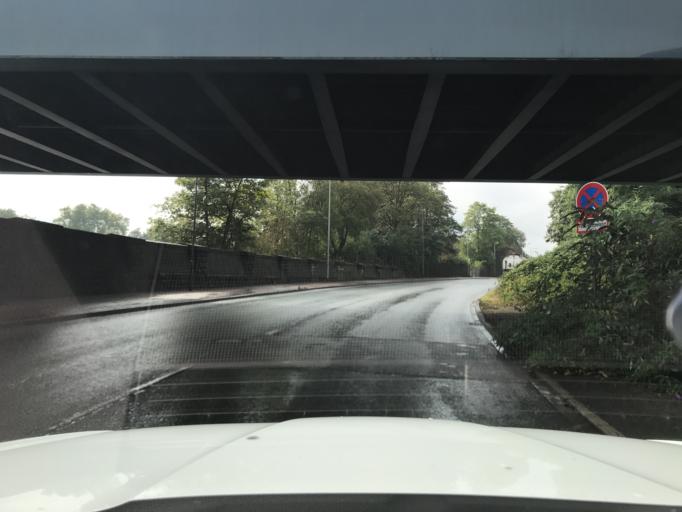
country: DE
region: North Rhine-Westphalia
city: Meiderich
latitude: 51.4605
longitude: 6.7976
